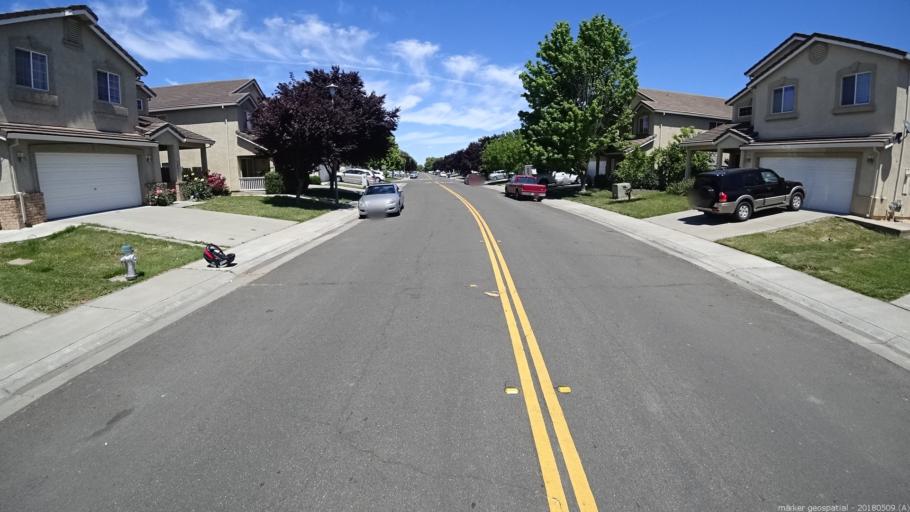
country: US
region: California
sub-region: Sacramento County
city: Sacramento
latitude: 38.6337
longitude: -121.5095
